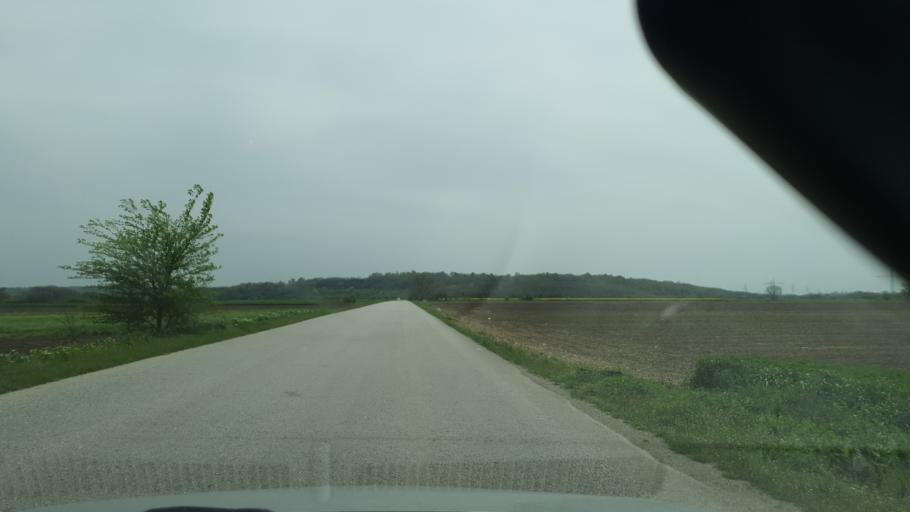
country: RS
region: Central Serbia
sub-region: Branicevski Okrug
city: Pozarevac
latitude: 44.6977
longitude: 21.1597
